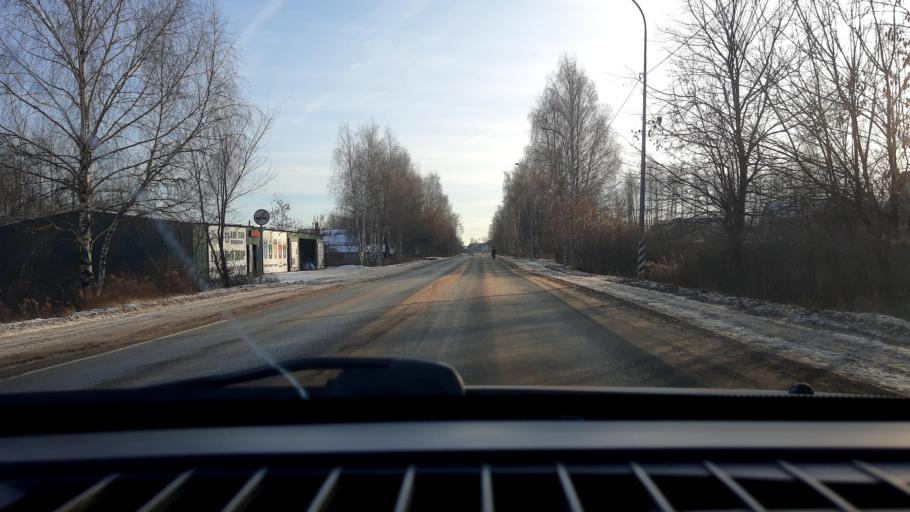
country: RU
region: Nizjnij Novgorod
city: Bor
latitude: 56.3816
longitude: 44.0380
